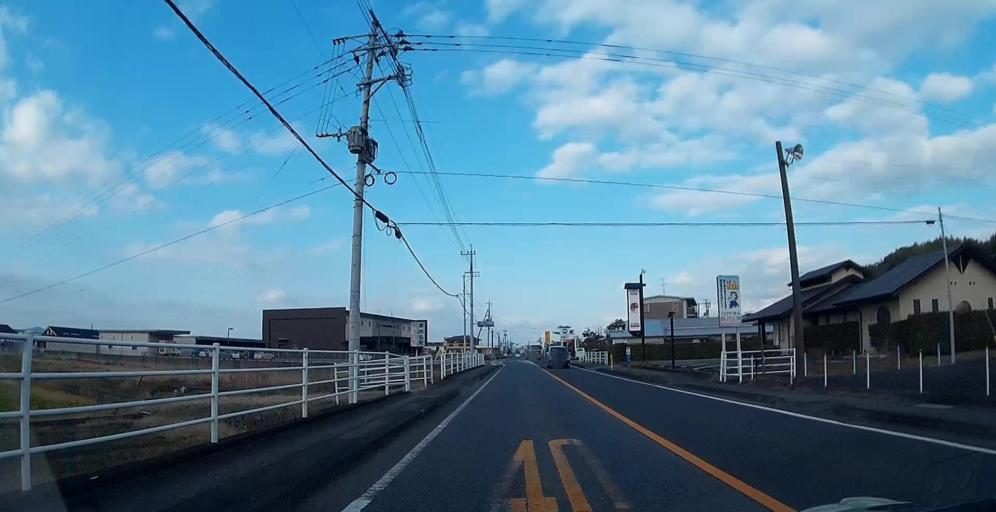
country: JP
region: Kumamoto
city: Yatsushiro
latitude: 32.5481
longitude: 130.6779
